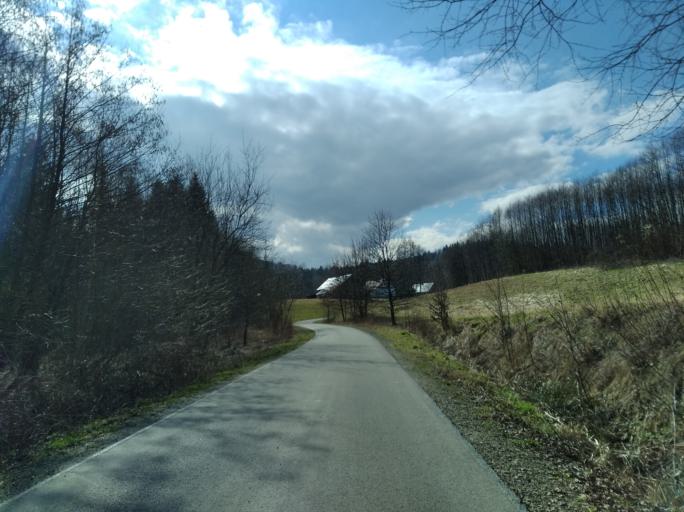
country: PL
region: Subcarpathian Voivodeship
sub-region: Powiat strzyzowski
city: Wysoka Strzyzowska
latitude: 49.8053
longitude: 21.7415
